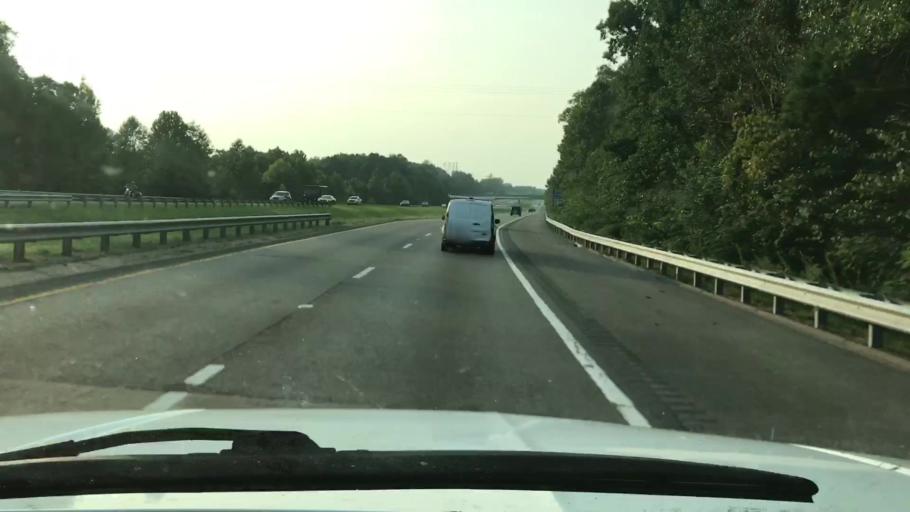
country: US
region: Virginia
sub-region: Chesterfield County
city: Brandermill
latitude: 37.4117
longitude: -77.6168
